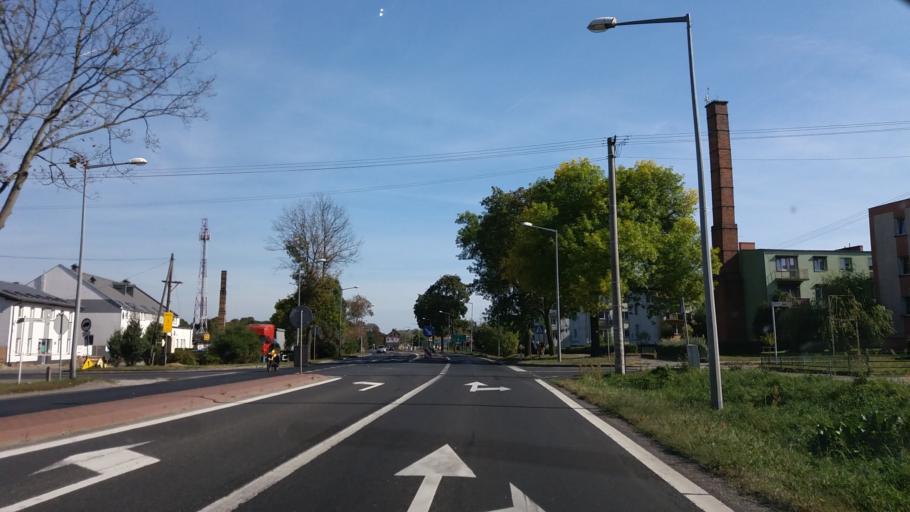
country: PL
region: Greater Poland Voivodeship
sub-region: Powiat miedzychodzki
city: Kwilcz
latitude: 52.5554
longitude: 16.0790
